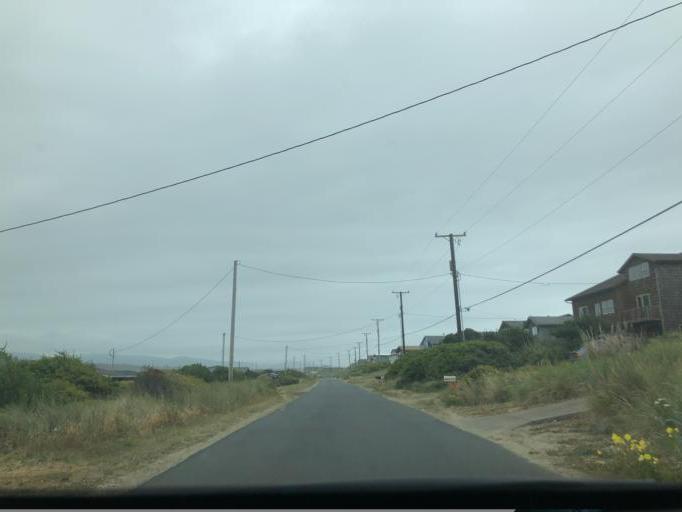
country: US
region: Oregon
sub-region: Lincoln County
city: Waldport
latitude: 44.4344
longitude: -124.0826
